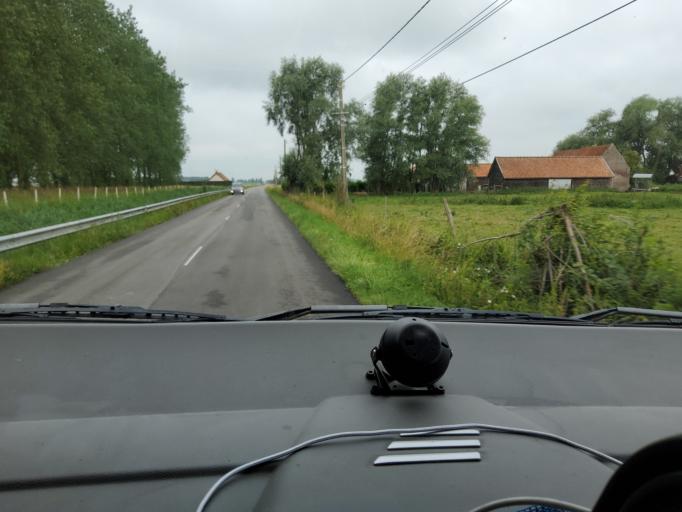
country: FR
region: Nord-Pas-de-Calais
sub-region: Departement du Pas-de-Calais
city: Sainte-Marie-Kerque
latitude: 50.9089
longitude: 2.1527
